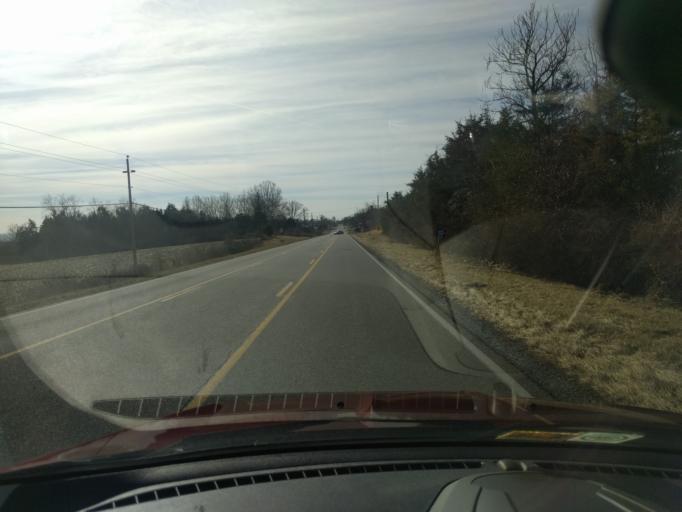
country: US
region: Virginia
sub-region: Augusta County
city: Weyers Cave
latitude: 38.2665
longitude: -78.9539
